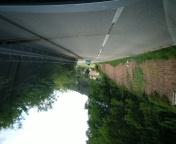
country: DE
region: Baden-Wuerttemberg
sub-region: Freiburg Region
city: Oppenau
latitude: 48.4364
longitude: 8.1727
